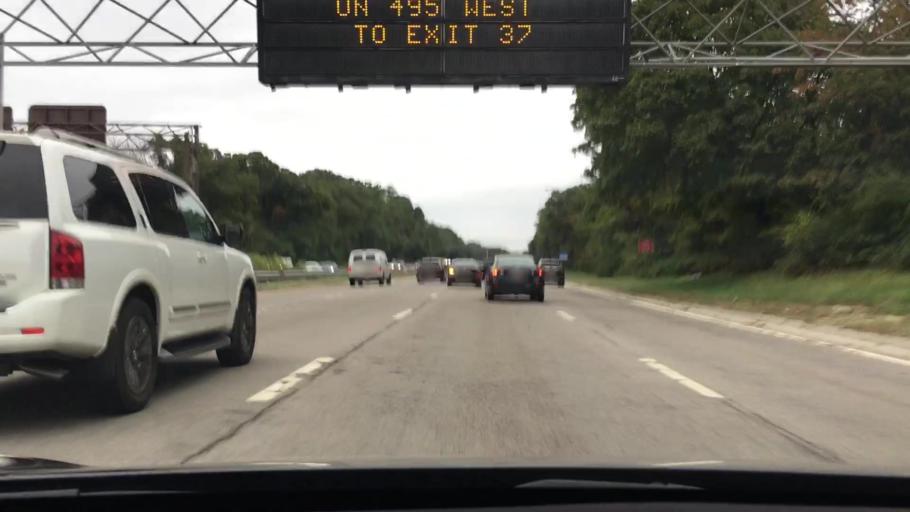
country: US
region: New York
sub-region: Nassau County
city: East Williston
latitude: 40.7643
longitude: -73.6250
